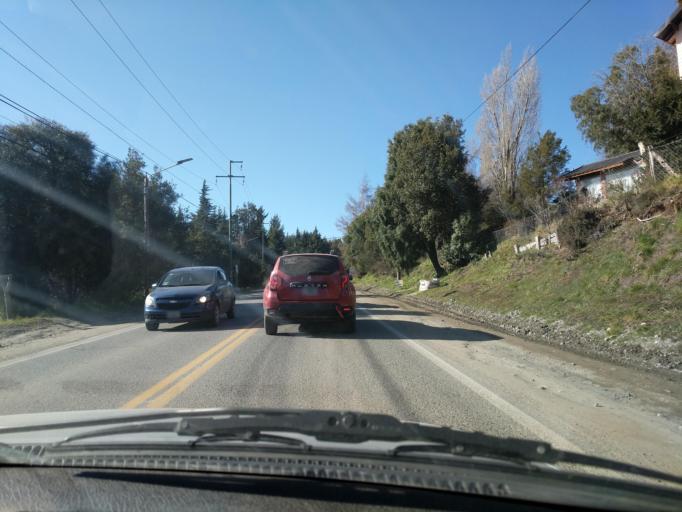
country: AR
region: Rio Negro
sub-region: Departamento de Bariloche
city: San Carlos de Bariloche
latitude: -41.1264
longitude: -71.3906
